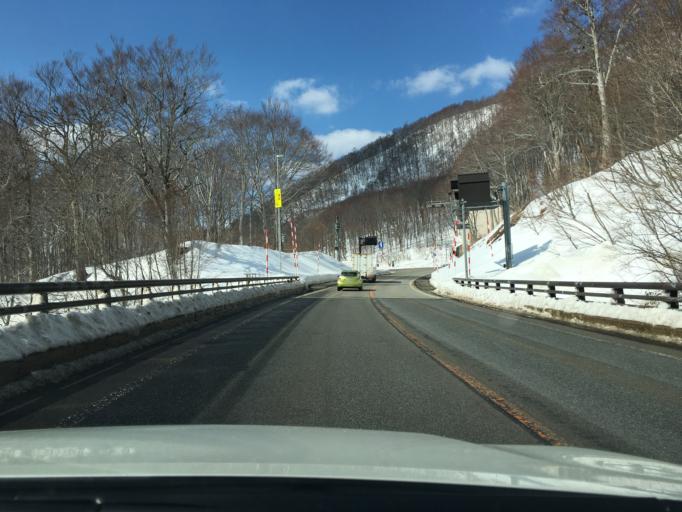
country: JP
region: Yamagata
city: Tsuruoka
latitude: 38.5379
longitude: 139.9335
